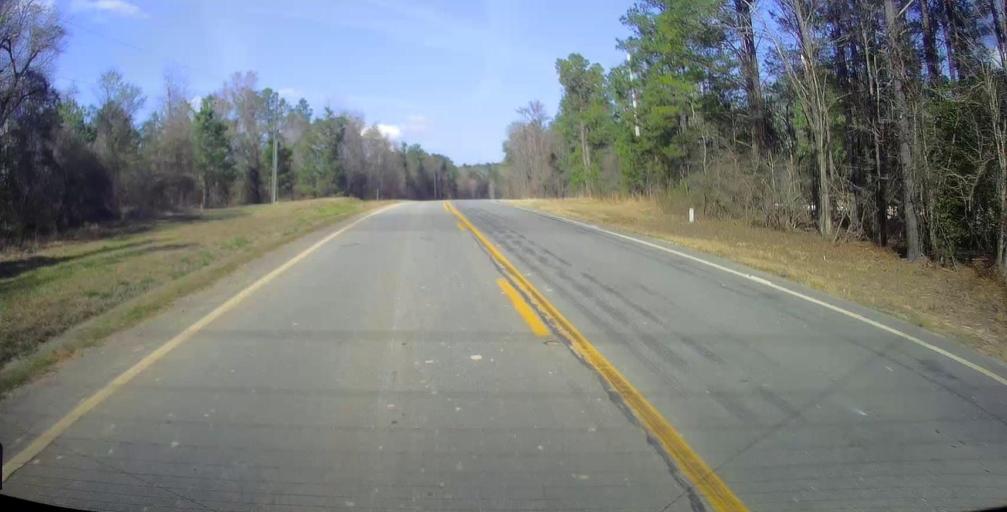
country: US
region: Georgia
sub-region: Wilkinson County
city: Gordon
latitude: 32.7960
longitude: -83.3310
